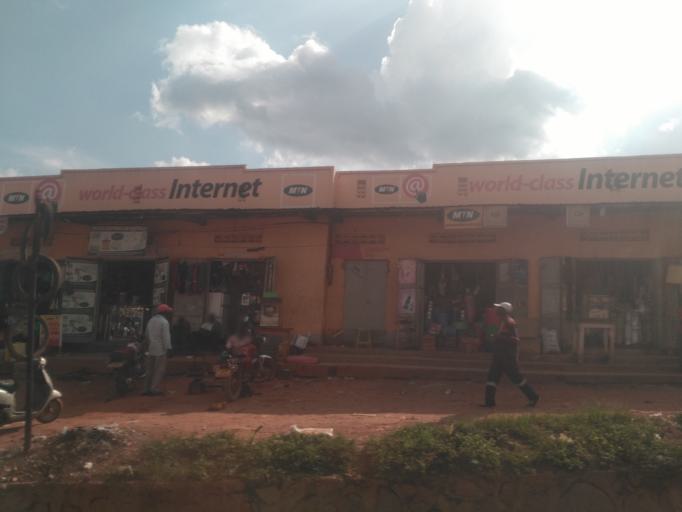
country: UG
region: Central Region
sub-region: Wakiso District
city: Kajansi
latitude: 0.2784
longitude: 32.4751
